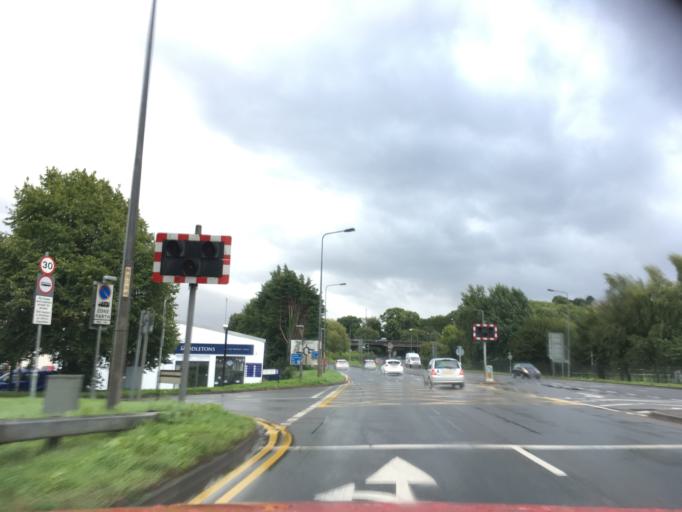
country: GB
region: Wales
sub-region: Newport
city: Newport
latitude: 51.6027
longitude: -3.0070
